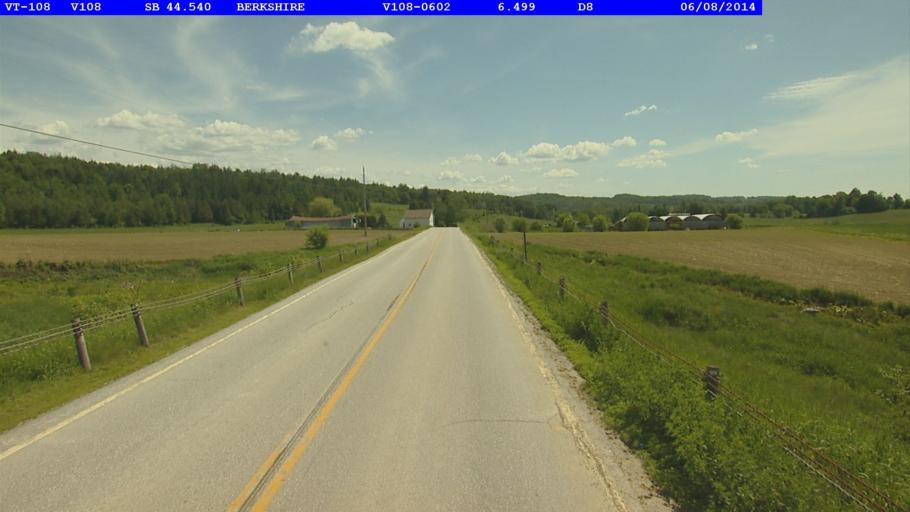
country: US
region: Vermont
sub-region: Franklin County
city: Enosburg Falls
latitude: 45.0106
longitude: -72.8248
